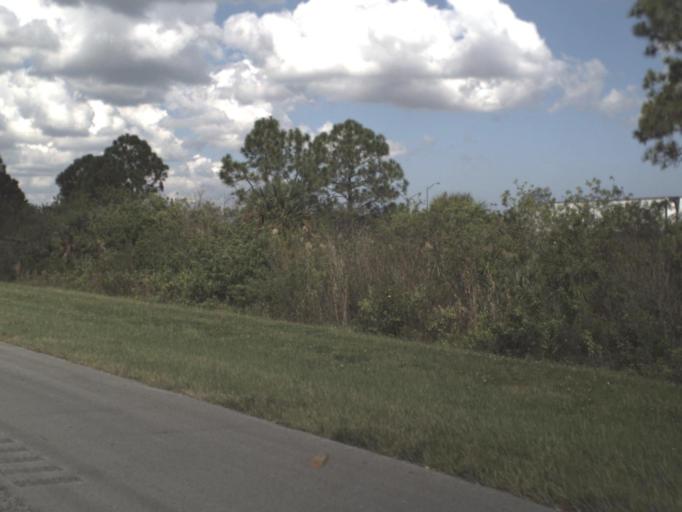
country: US
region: Florida
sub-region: Palm Beach County
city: Tequesta
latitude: 27.0013
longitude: -80.2037
